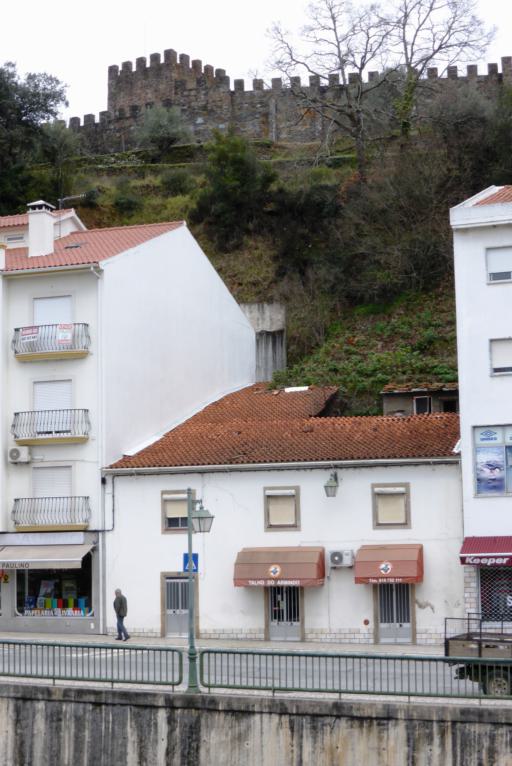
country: PT
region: Castelo Branco
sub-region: Serta
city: Serta
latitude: 39.8044
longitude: -8.1000
